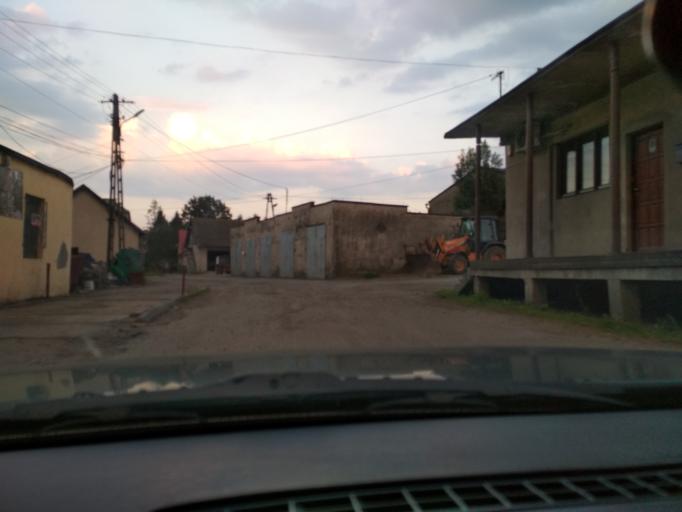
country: PL
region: Silesian Voivodeship
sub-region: Powiat bielski
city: Jasienica
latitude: 49.8375
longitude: 18.9369
